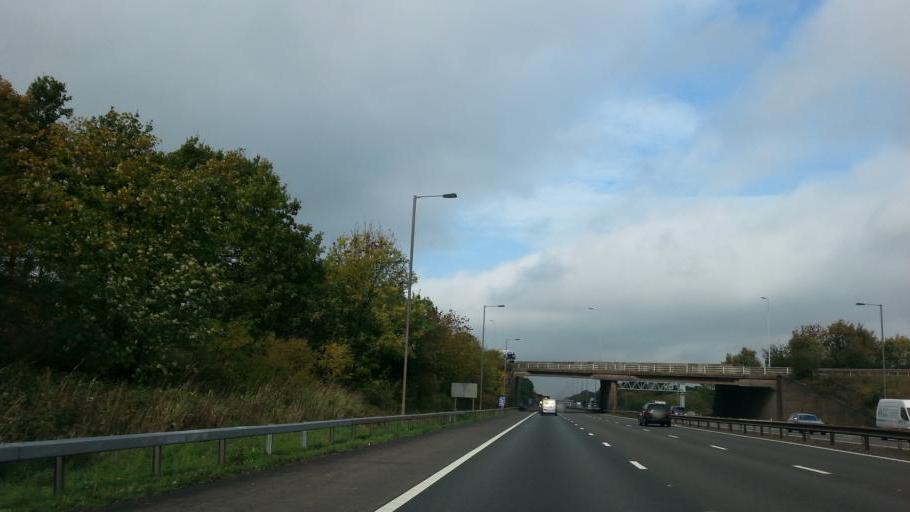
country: GB
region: England
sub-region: Staffordshire
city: Essington
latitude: 52.6355
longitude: -2.0524
